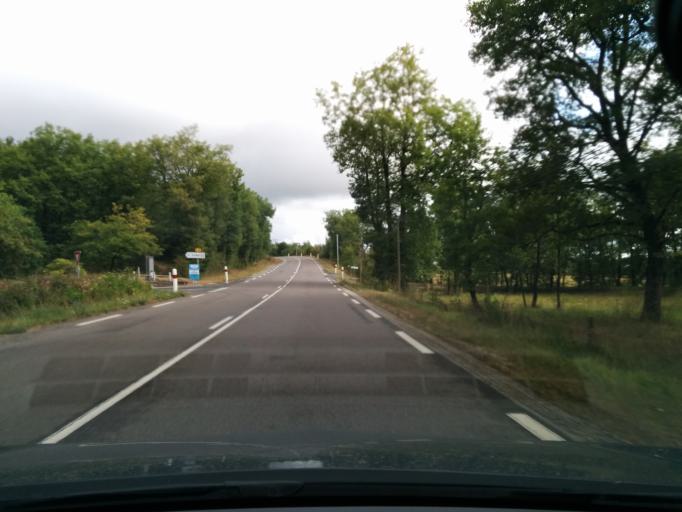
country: FR
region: Midi-Pyrenees
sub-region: Departement du Lot
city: Souillac
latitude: 44.9839
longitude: 1.5097
